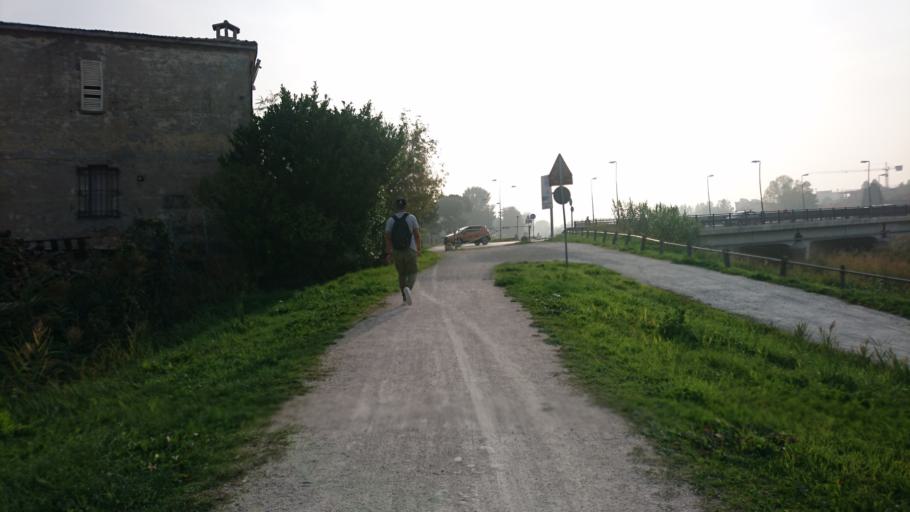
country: IT
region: Emilia-Romagna
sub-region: Provincia di Rimini
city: Rimini
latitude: 44.0677
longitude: 12.5567
